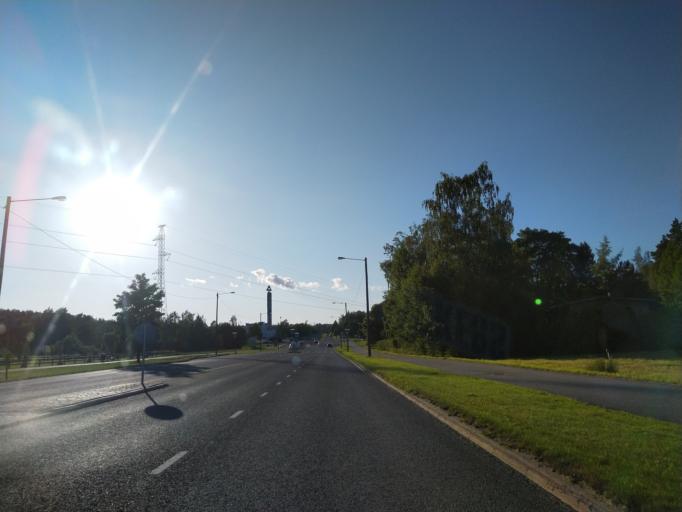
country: FI
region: Varsinais-Suomi
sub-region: Turku
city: Kaarina
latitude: 60.4442
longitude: 22.3317
